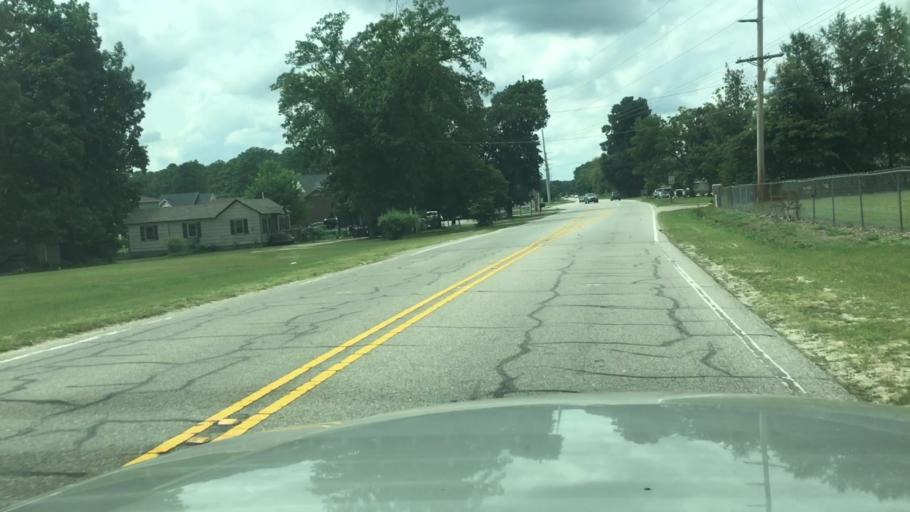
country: US
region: North Carolina
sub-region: Cumberland County
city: Hope Mills
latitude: 35.0046
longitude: -78.9966
